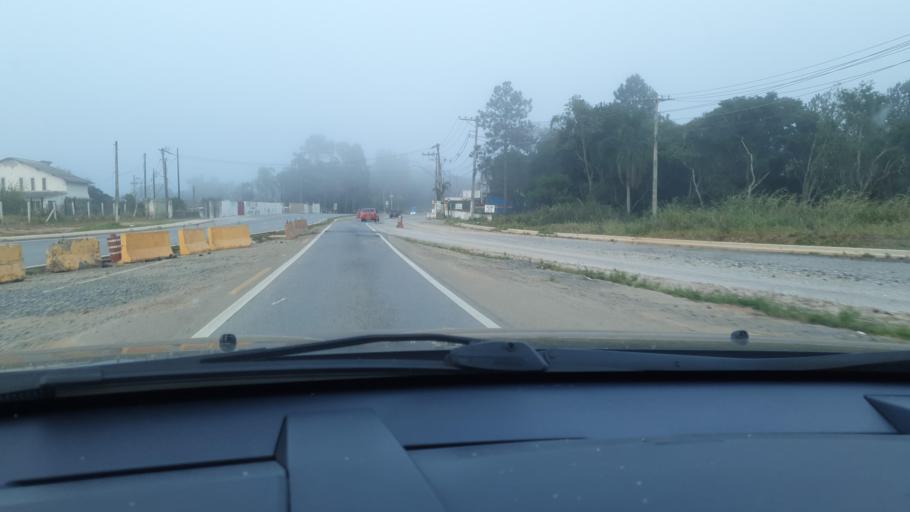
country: BR
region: Sao Paulo
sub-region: Ibiuna
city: Ibiuna
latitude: -23.6529
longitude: -47.1818
